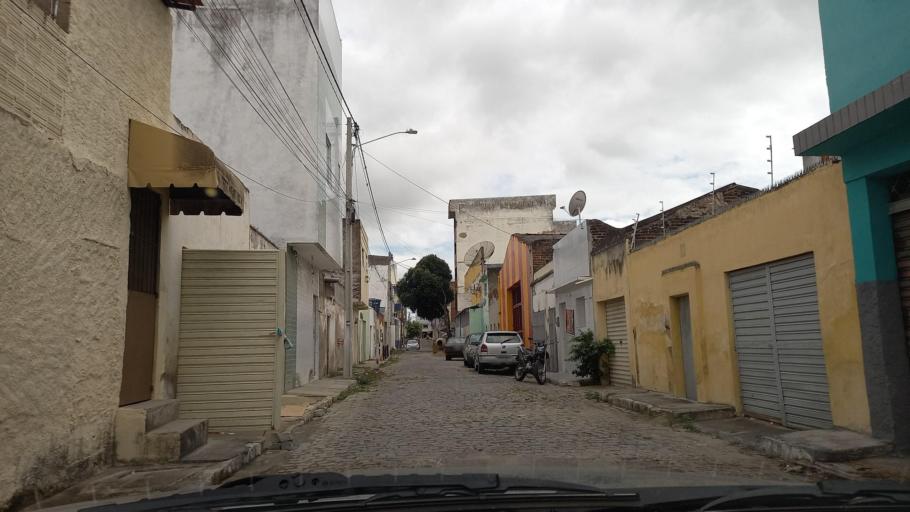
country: BR
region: Pernambuco
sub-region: Caruaru
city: Caruaru
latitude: -8.2803
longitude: -35.9748
